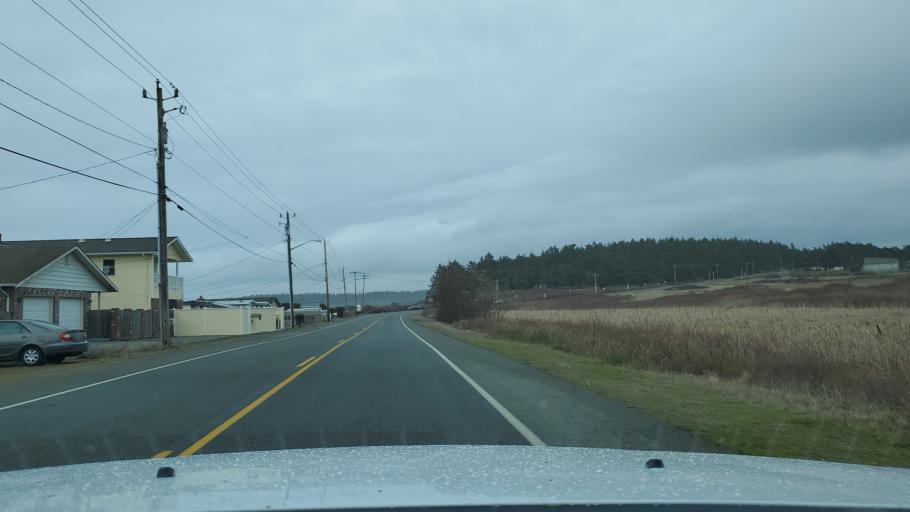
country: US
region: Washington
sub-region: Island County
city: Ault Field
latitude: 48.3065
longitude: -122.7182
